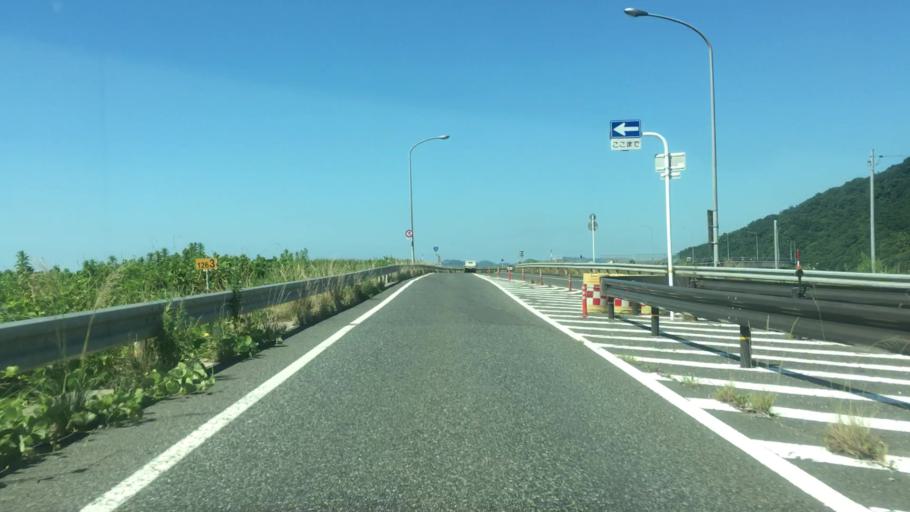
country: JP
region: Tottori
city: Tottori
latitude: 35.4358
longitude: 134.2050
